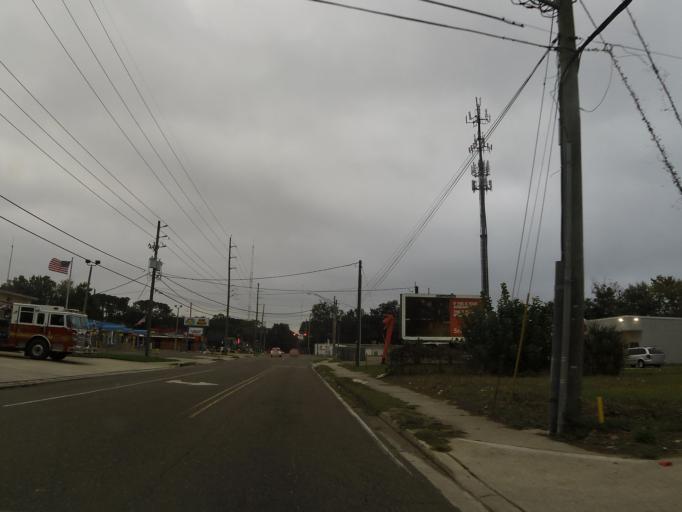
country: US
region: Florida
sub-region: Clay County
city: Bellair-Meadowbrook Terrace
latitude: 30.2808
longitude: -81.7479
